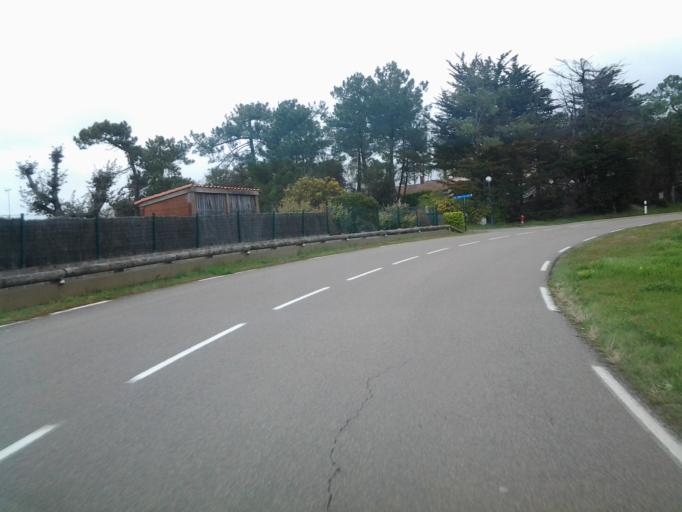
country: FR
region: Pays de la Loire
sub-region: Departement de la Vendee
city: Longeville-sur-Mer
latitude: 46.3945
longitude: -1.4851
